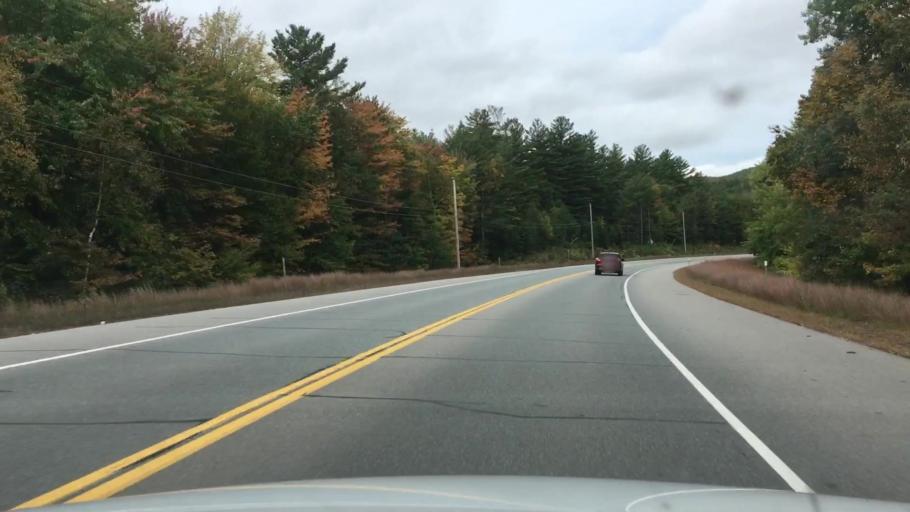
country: US
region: New Hampshire
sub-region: Coos County
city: Gorham
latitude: 44.3924
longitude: -71.0464
